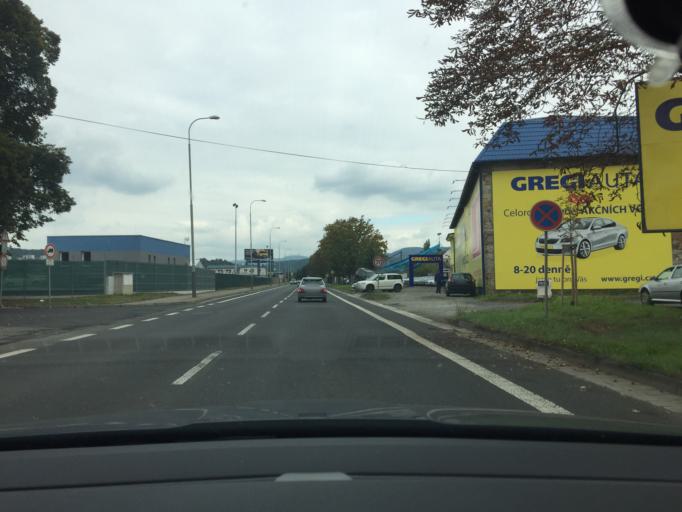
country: CZ
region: Ustecky
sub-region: Okres Usti nad Labem
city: Usti nad Labem
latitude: 50.6619
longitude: 14.0641
